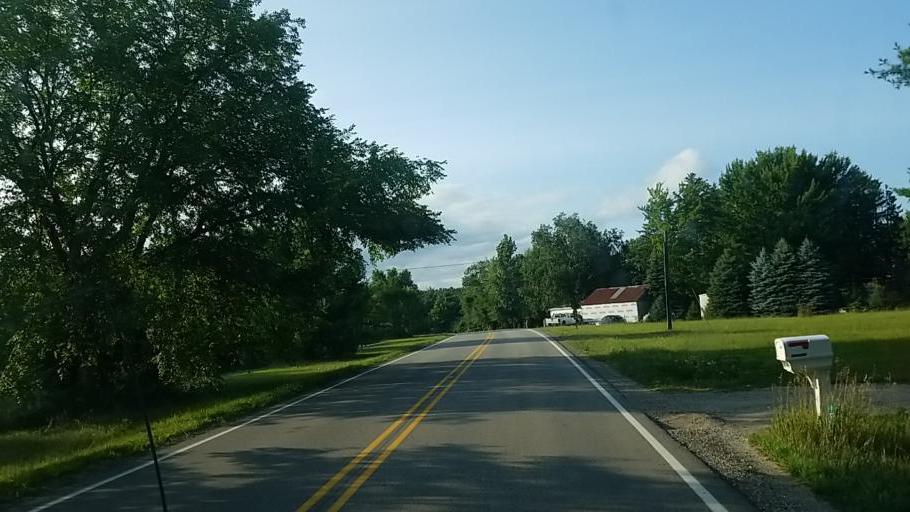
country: US
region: Michigan
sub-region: Montcalm County
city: Greenville
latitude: 43.2430
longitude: -85.3693
